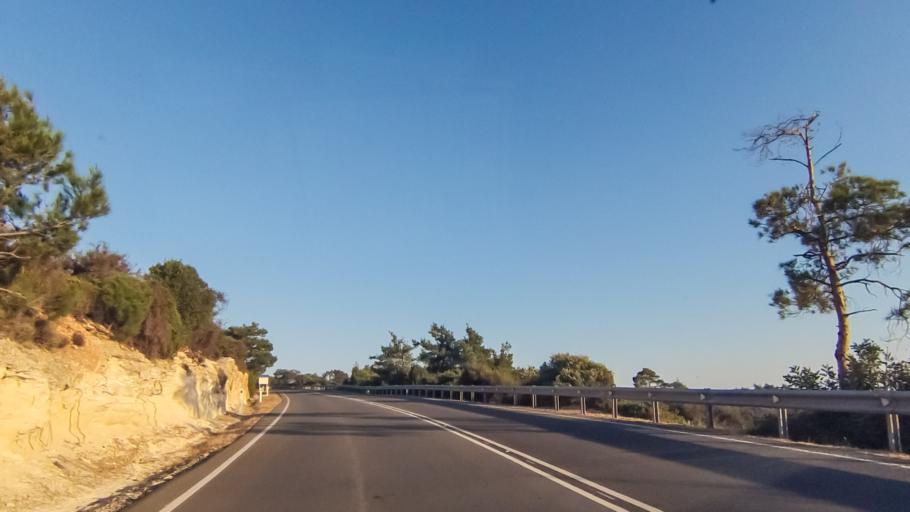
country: CY
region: Limassol
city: Sotira
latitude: 34.6750
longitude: 32.8518
